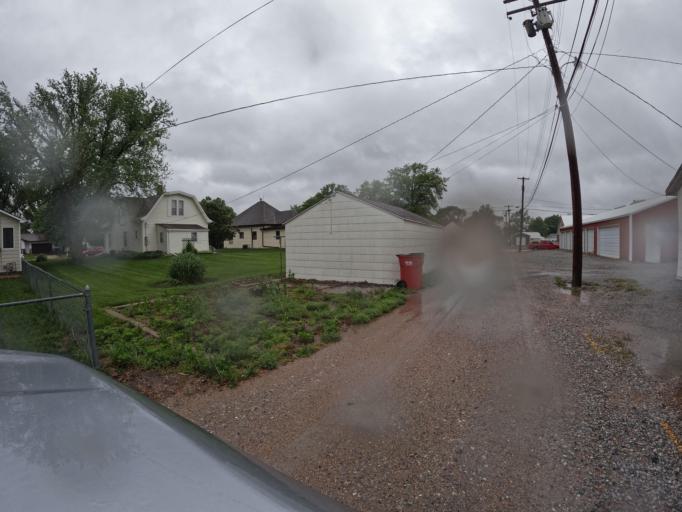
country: US
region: Nebraska
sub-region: Saline County
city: Wilber
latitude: 40.3940
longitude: -96.9209
